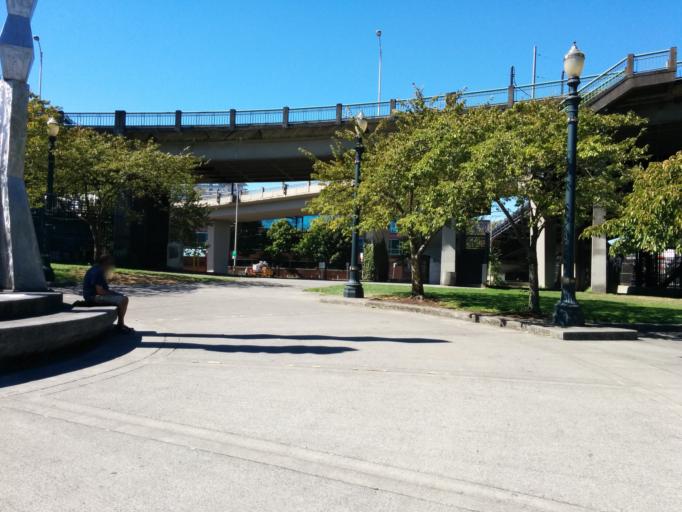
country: US
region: Oregon
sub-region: Multnomah County
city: Portland
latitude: 45.5266
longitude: -122.6703
